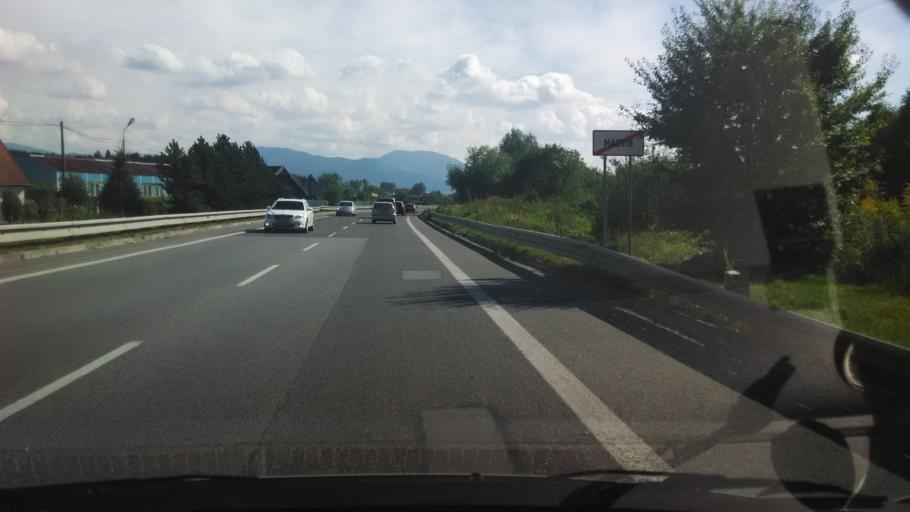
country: SK
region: Zilinsky
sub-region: Okres Martin
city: Martin
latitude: 49.0502
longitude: 18.9070
